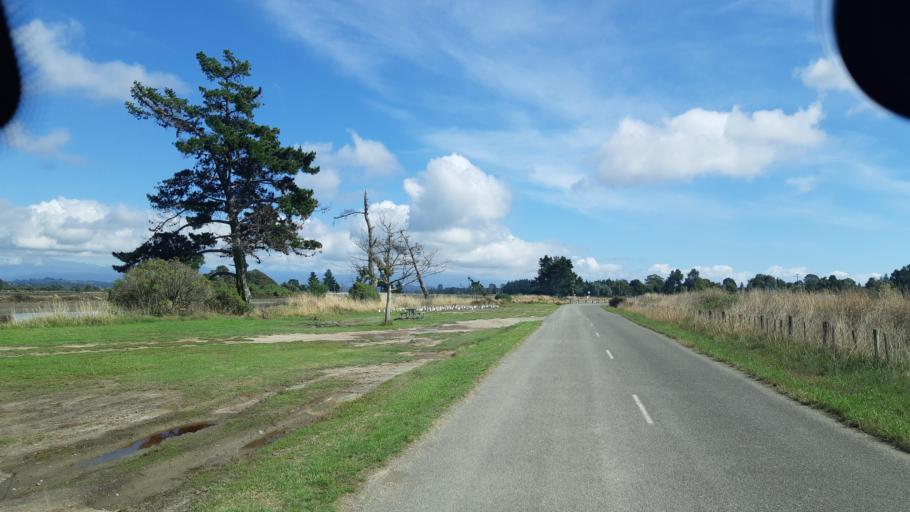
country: NZ
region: Tasman
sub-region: Tasman District
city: Richmond
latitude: -41.2982
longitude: 173.1556
